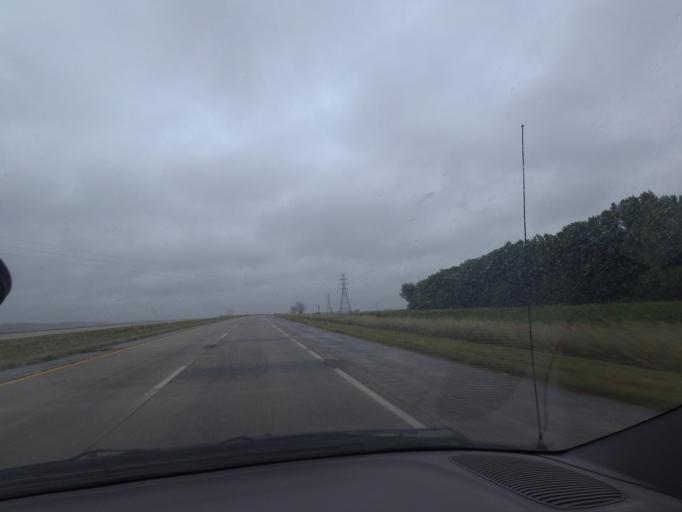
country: US
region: Illinois
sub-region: Adams County
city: Payson
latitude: 39.7329
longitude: -91.2387
